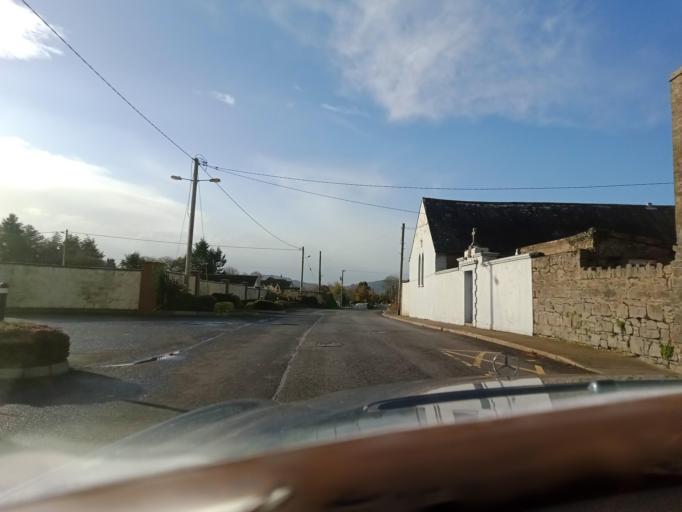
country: IE
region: Leinster
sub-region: Kilkenny
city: Mooncoin
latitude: 52.2952
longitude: -7.2605
